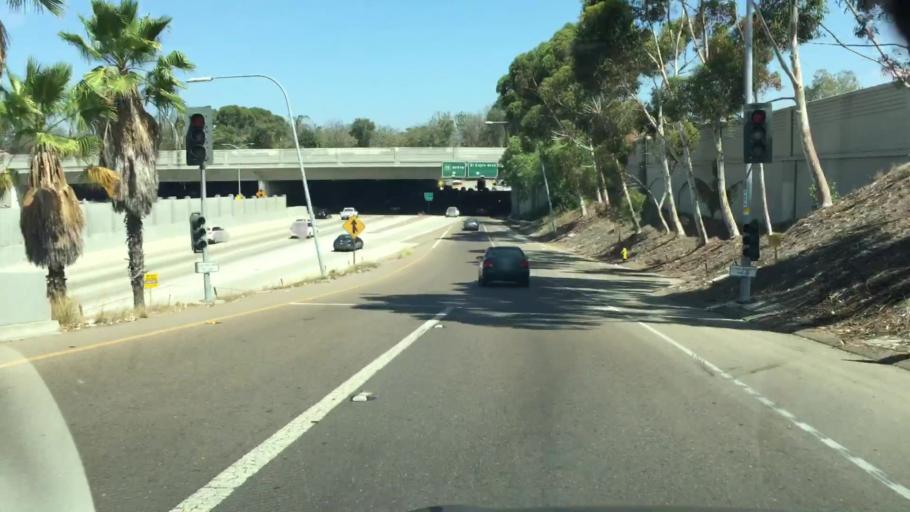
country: US
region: California
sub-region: San Diego County
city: San Diego
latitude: 32.7501
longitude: -117.1083
